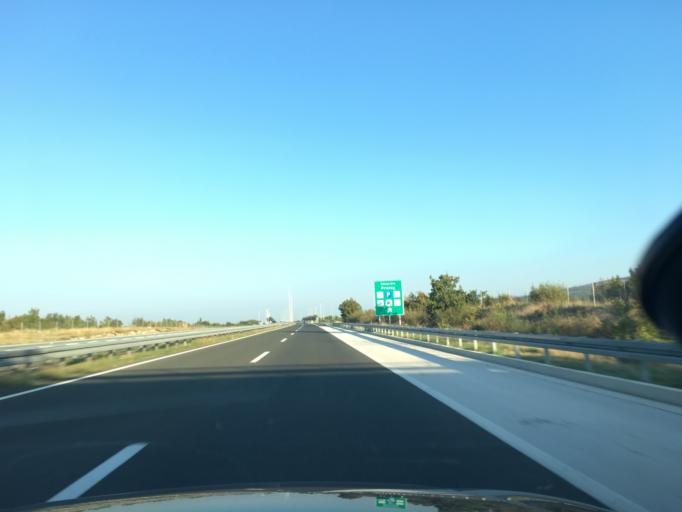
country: HR
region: Sibensko-Kniniska
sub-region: Grad Sibenik
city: Pirovac
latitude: 43.9406
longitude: 15.7013
